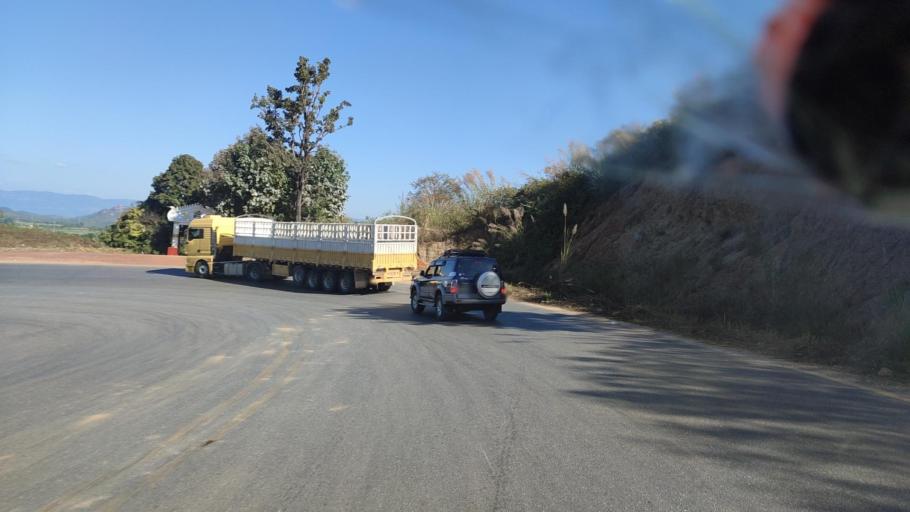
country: MM
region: Mandalay
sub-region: Pyin Oo Lwin District
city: Pyin Oo Lwin
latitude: 22.0776
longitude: 96.5818
